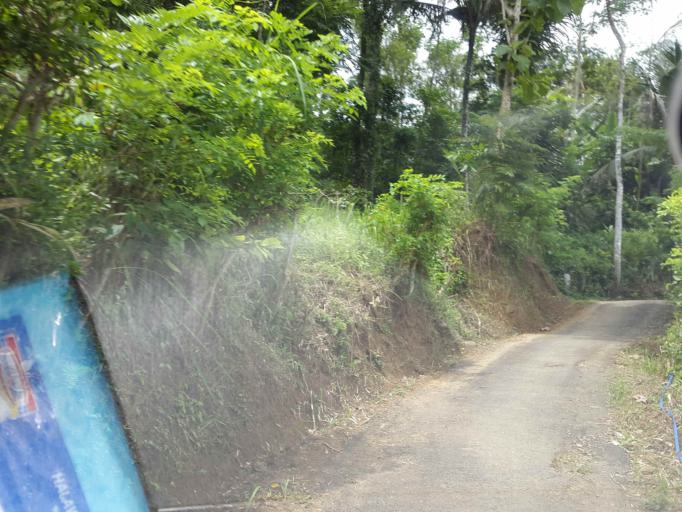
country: ID
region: Central Java
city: Muara
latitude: -7.2649
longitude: 108.8877
